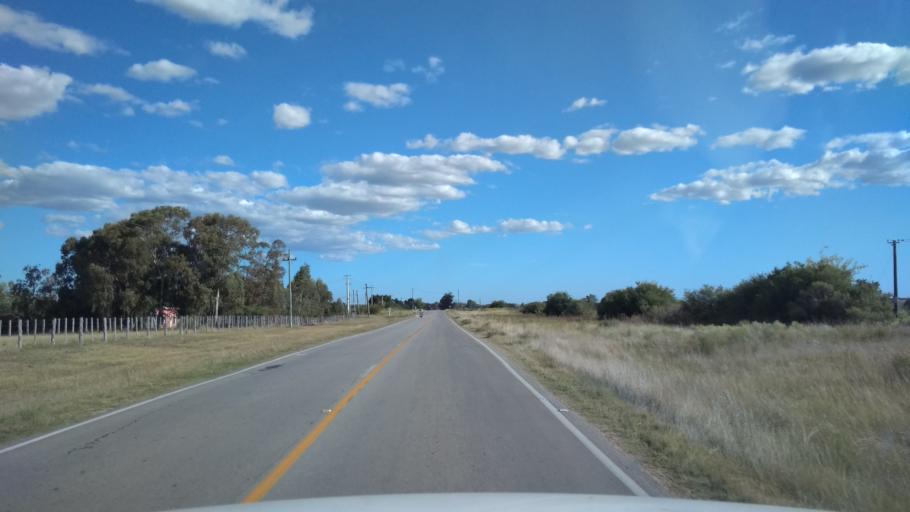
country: UY
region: Canelones
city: San Ramon
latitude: -34.3404
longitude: -55.9598
